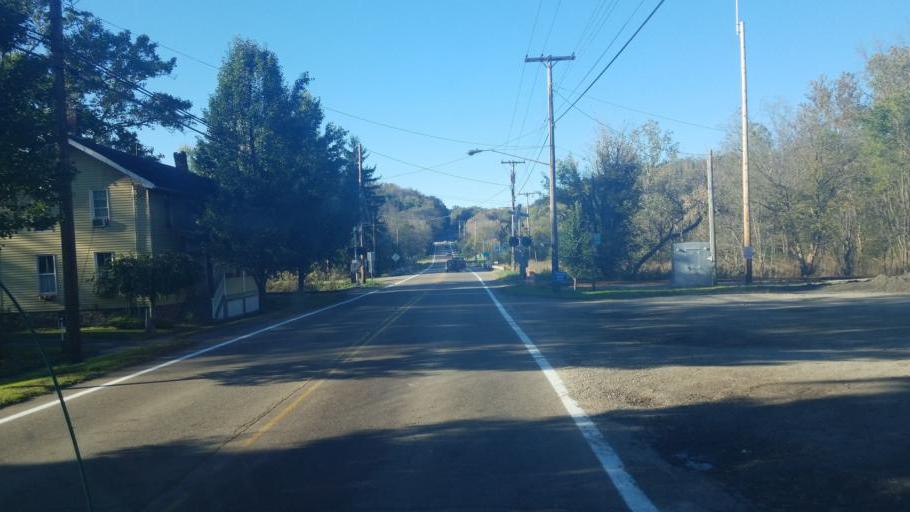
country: US
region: Ohio
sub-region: Columbiana County
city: New Waterford
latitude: 40.7929
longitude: -80.6270
